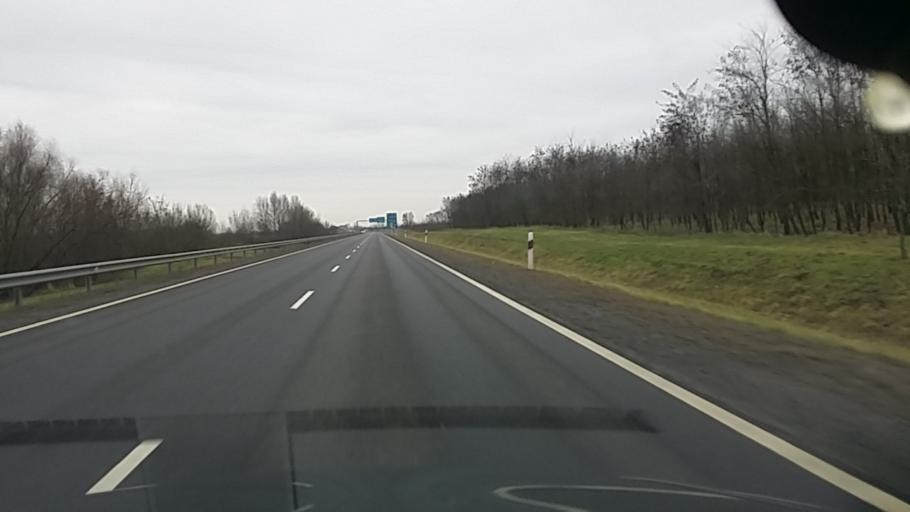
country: HU
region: Szabolcs-Szatmar-Bereg
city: Nagykallo
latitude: 47.9065
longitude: 21.8178
